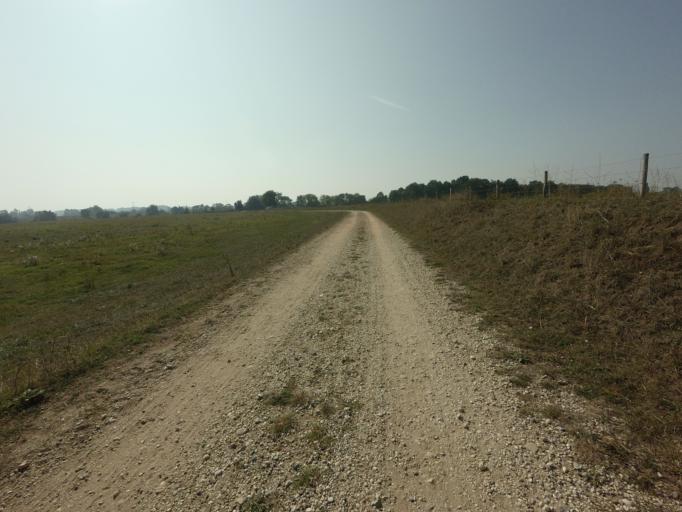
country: NL
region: Limburg
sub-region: Gemeente Roermond
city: Leeuwen
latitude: 51.2322
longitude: 5.9948
